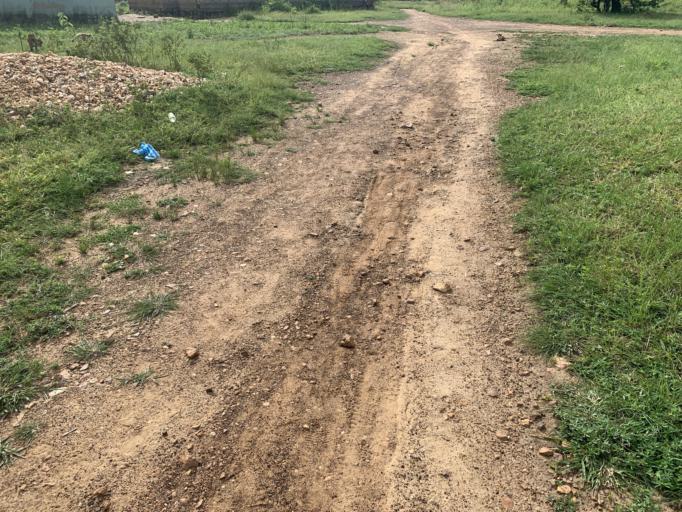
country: GH
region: Upper East
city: Navrongo
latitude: 10.8703
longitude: -1.0724
